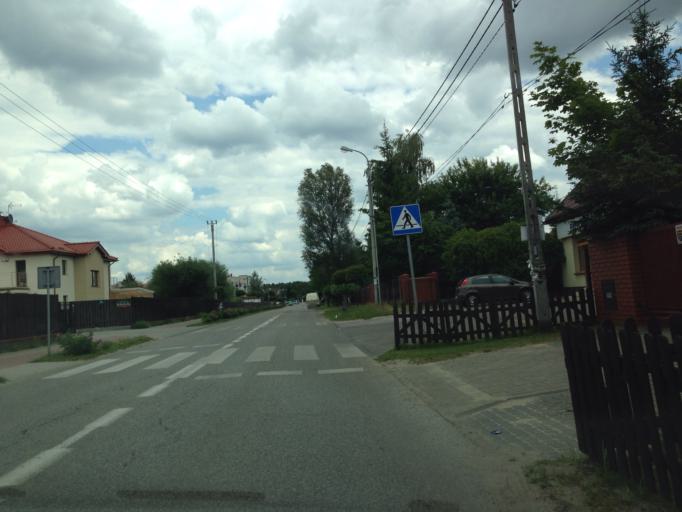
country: PL
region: Masovian Voivodeship
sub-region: Powiat warszawski zachodni
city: Babice
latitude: 52.2510
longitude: 20.8535
